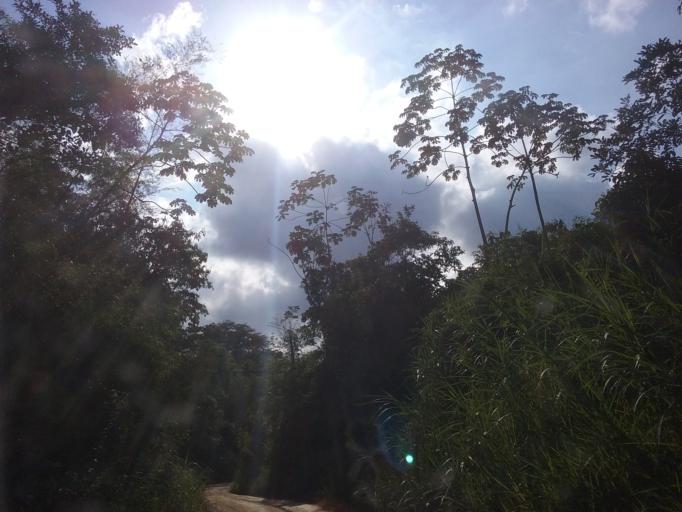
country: CO
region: Tolima
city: Libano
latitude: 4.8953
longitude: -75.0299
